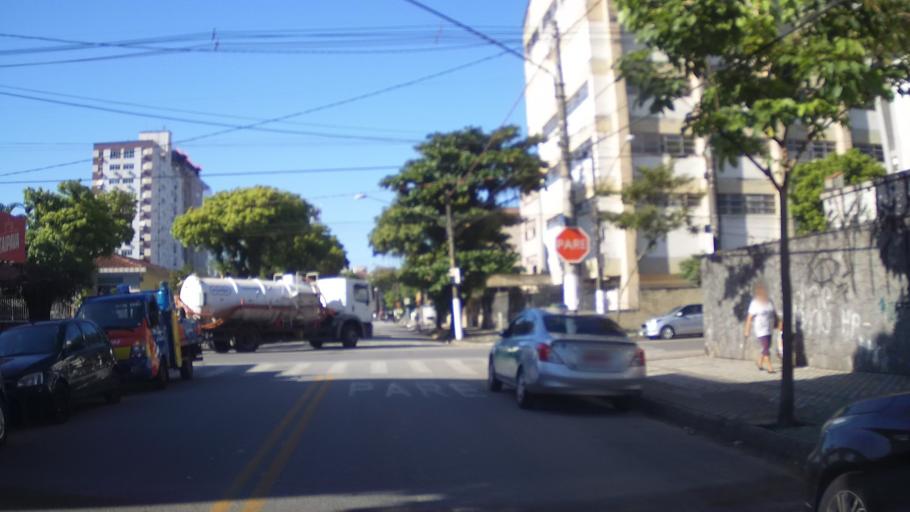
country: BR
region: Sao Paulo
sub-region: Santos
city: Santos
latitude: -23.9534
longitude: -46.3465
